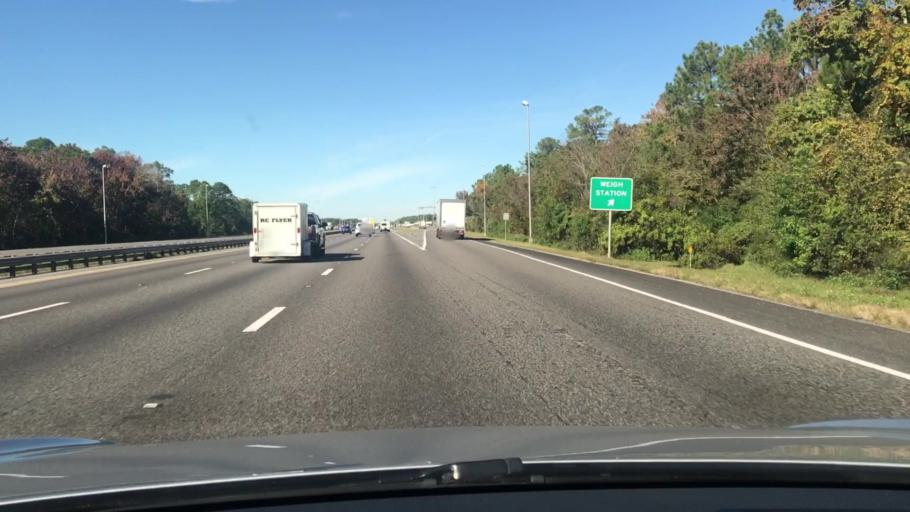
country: US
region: Florida
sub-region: Flagler County
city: Flagler Beach
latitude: 29.5020
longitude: -81.1936
